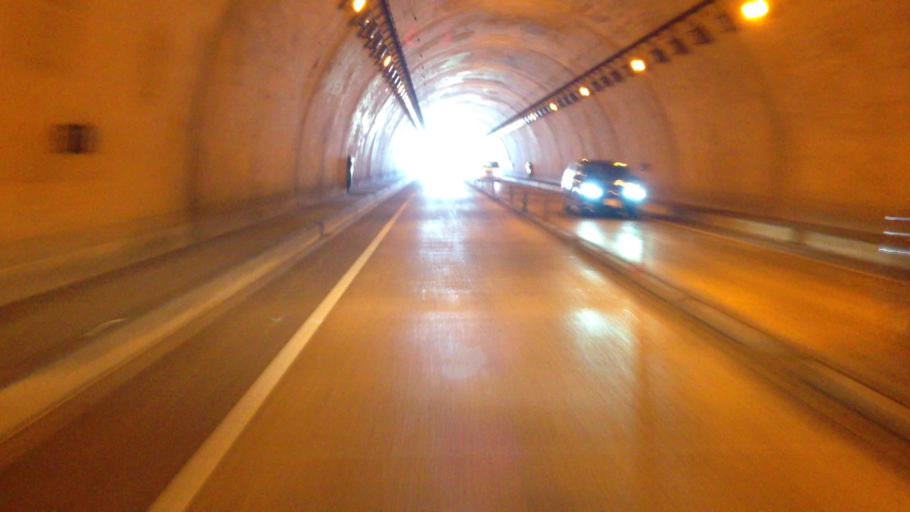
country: JP
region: Kanagawa
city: Yokosuka
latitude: 35.2390
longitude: 139.6530
